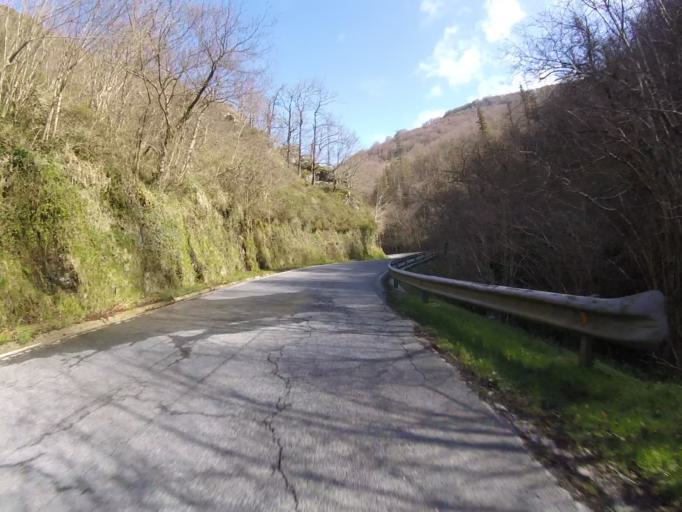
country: ES
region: Navarre
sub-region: Provincia de Navarra
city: Ezkurra
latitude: 43.0955
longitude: -1.8653
